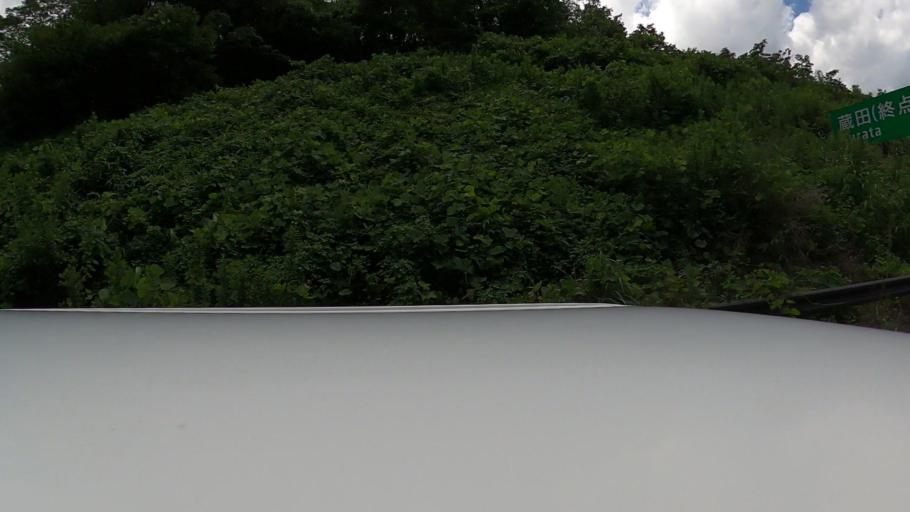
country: JP
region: Miyazaki
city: Nobeoka
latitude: 32.5841
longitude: 131.5151
